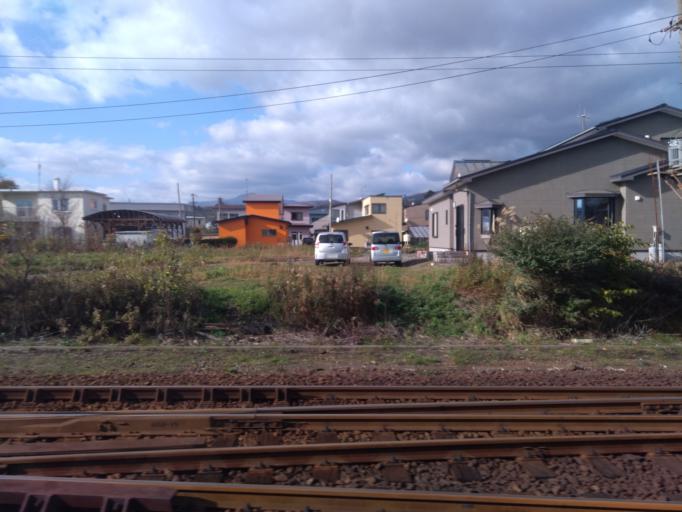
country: JP
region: Hokkaido
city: Shiraoi
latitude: 42.4504
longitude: 141.1779
